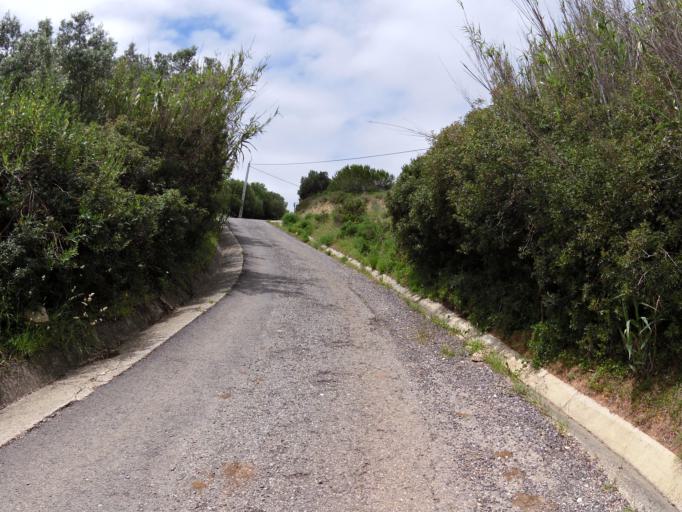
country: PT
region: Faro
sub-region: Vila do Bispo
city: Vila do Bispo
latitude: 37.0737
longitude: -8.8748
